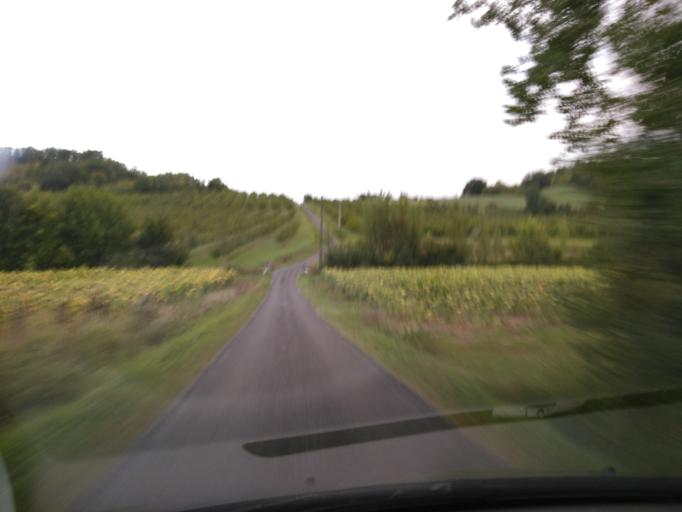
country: FR
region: Aquitaine
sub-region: Departement du Lot-et-Garonne
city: Saint-Hilaire
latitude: 44.5154
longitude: 0.6835
